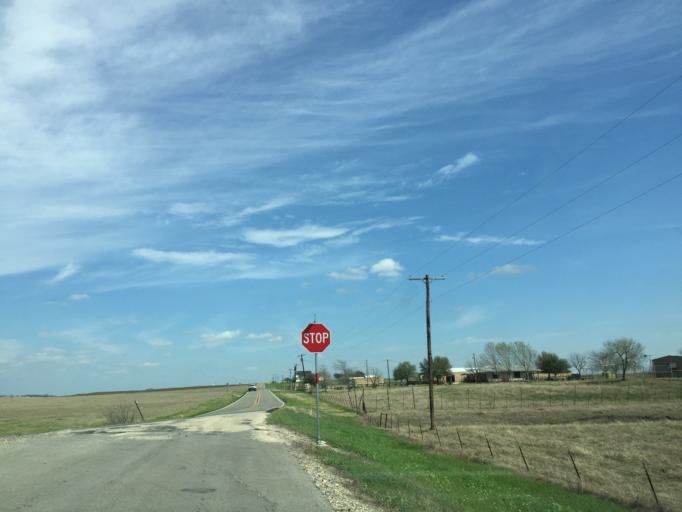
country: US
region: Texas
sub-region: Williamson County
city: Taylor
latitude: 30.5537
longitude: -97.3215
